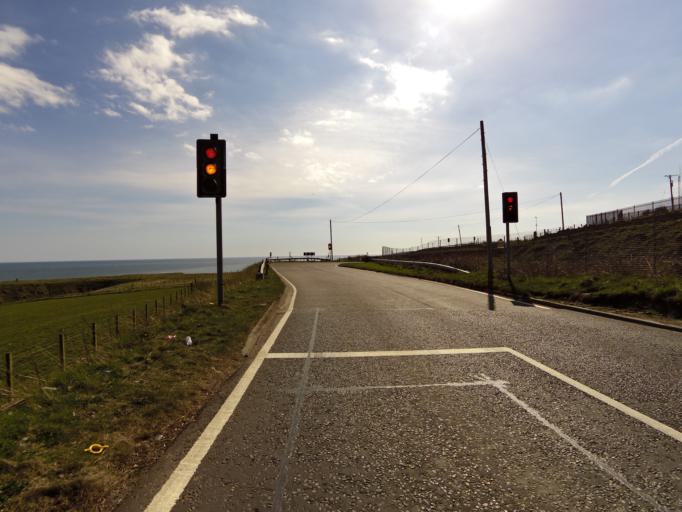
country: GB
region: Scotland
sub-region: Aberdeen City
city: Aberdeen
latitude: 57.1259
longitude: -2.0541
